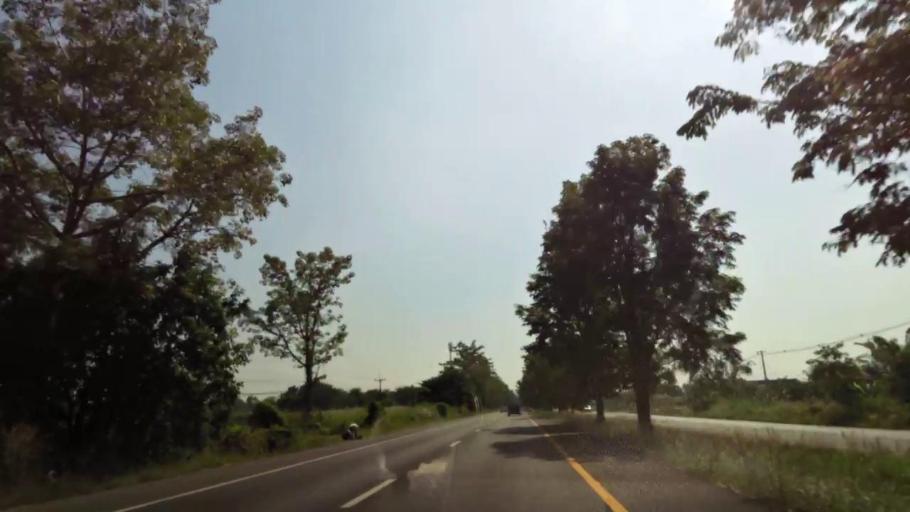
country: TH
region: Nakhon Sawan
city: Kao Liao
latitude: 15.9701
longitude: 100.1195
